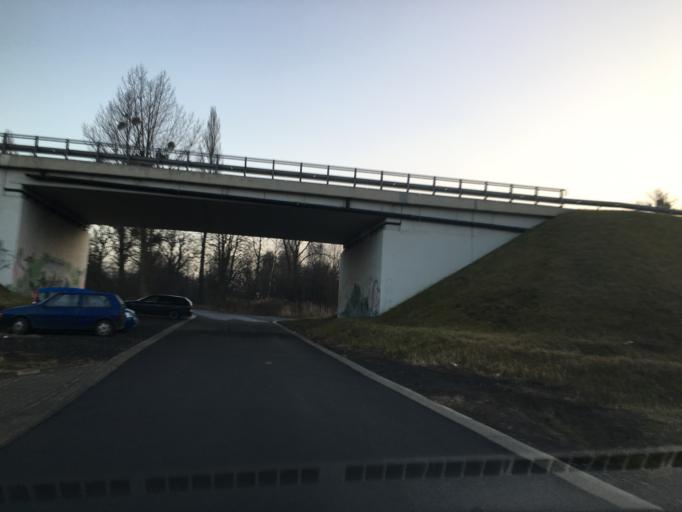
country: PL
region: Silesian Voivodeship
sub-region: Powiat tarnogorski
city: Radzionkow
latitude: 50.3686
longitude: 18.8873
